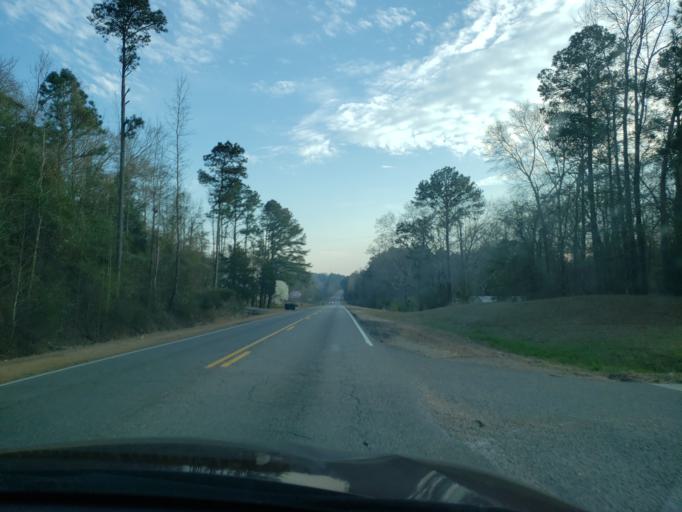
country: US
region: Alabama
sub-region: Hale County
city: Greensboro
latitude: 32.7437
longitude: -87.5853
